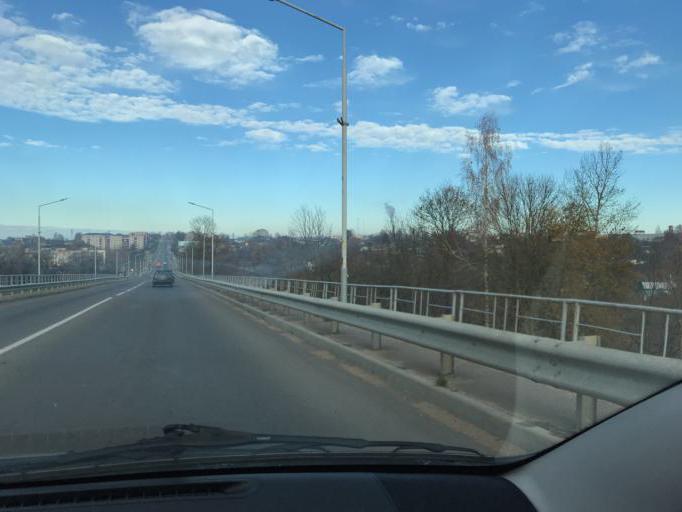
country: BY
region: Vitebsk
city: Haradok
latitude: 55.4641
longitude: 29.9817
